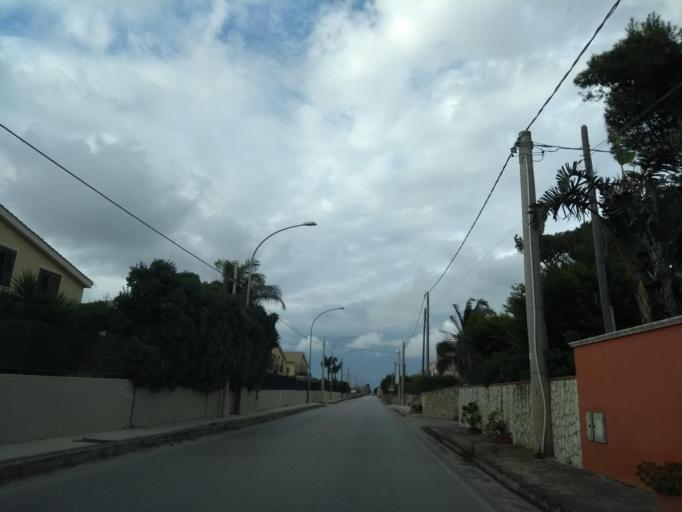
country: IT
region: Sicily
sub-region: Trapani
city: Marausa
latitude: 37.9575
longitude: 12.5169
